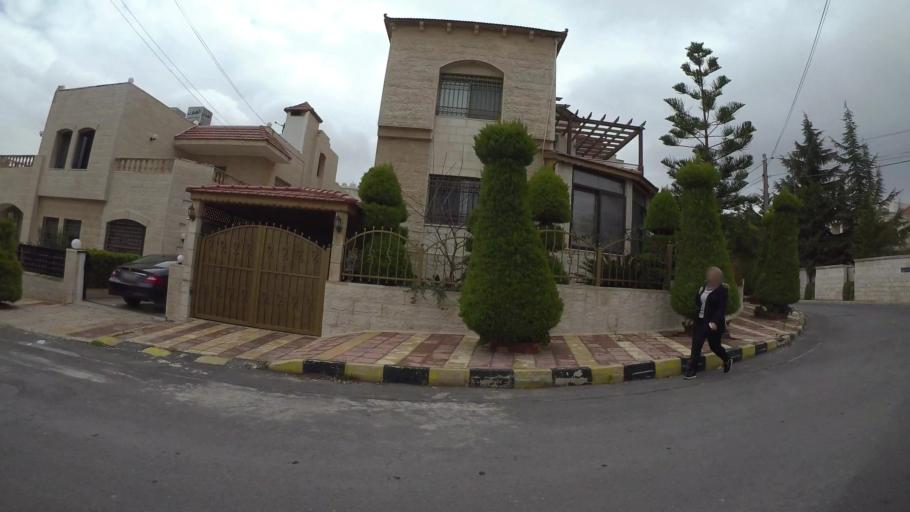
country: JO
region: Amman
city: Wadi as Sir
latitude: 31.9674
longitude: 35.8280
